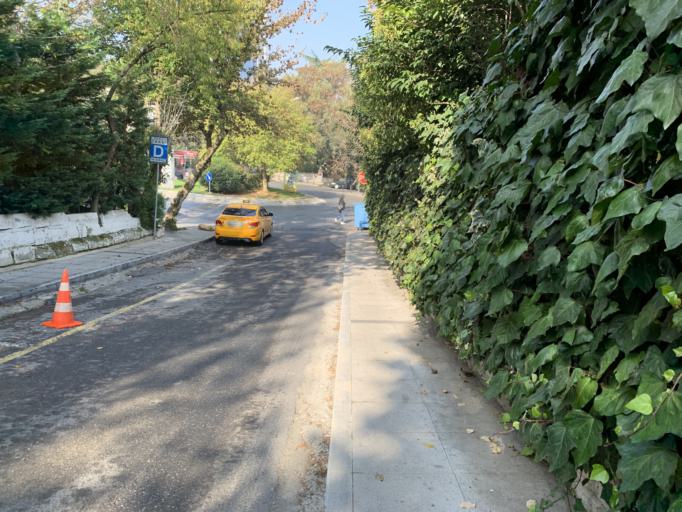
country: TR
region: Istanbul
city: Sisli
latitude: 41.0831
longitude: 29.0148
